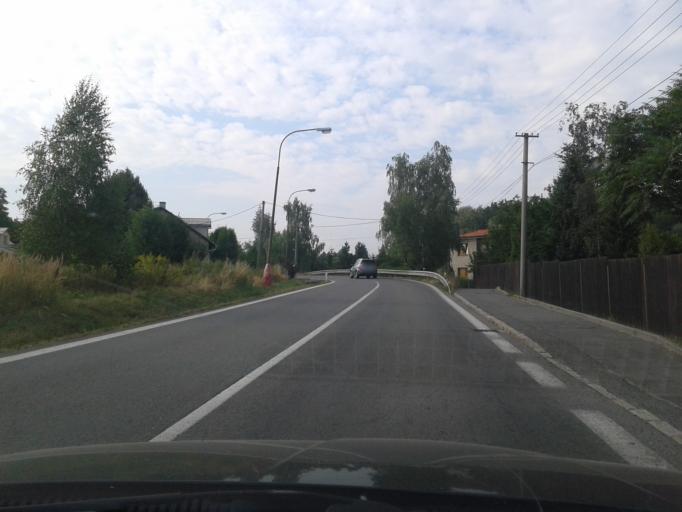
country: CZ
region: Moravskoslezsky
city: Orlova
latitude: 49.8702
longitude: 18.4427
